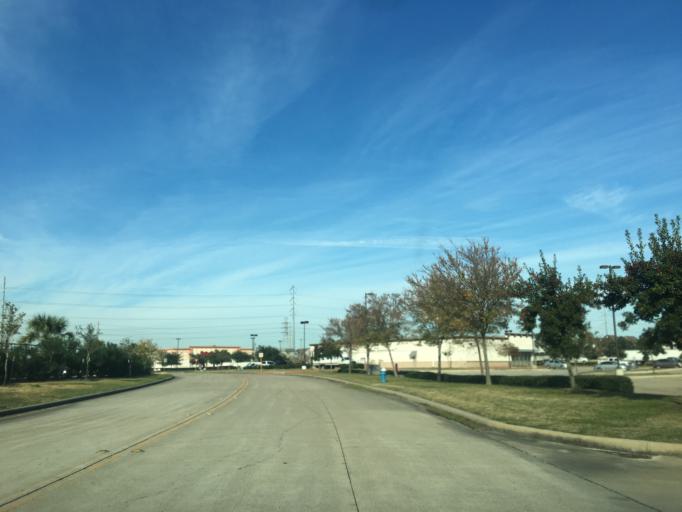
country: US
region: Texas
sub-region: Harris County
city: Cloverleaf
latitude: 29.8143
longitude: -95.1661
